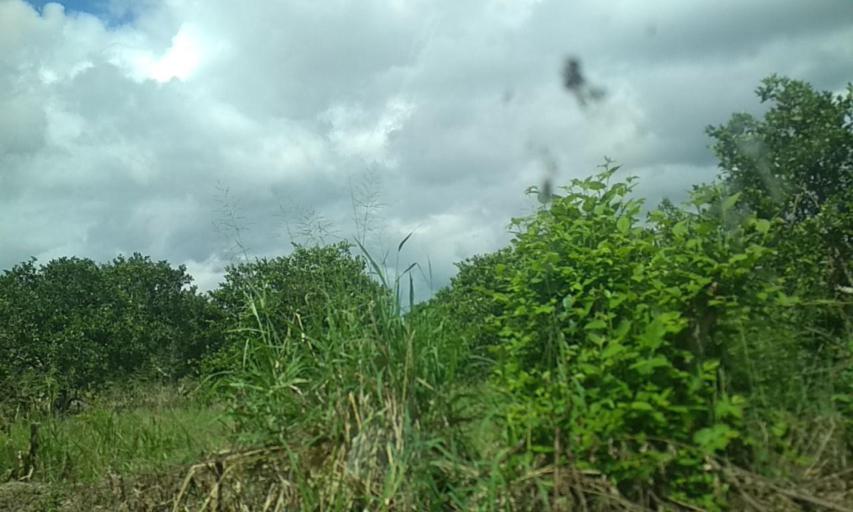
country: MX
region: Puebla
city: San Jose Acateno
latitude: 20.2792
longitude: -97.1315
